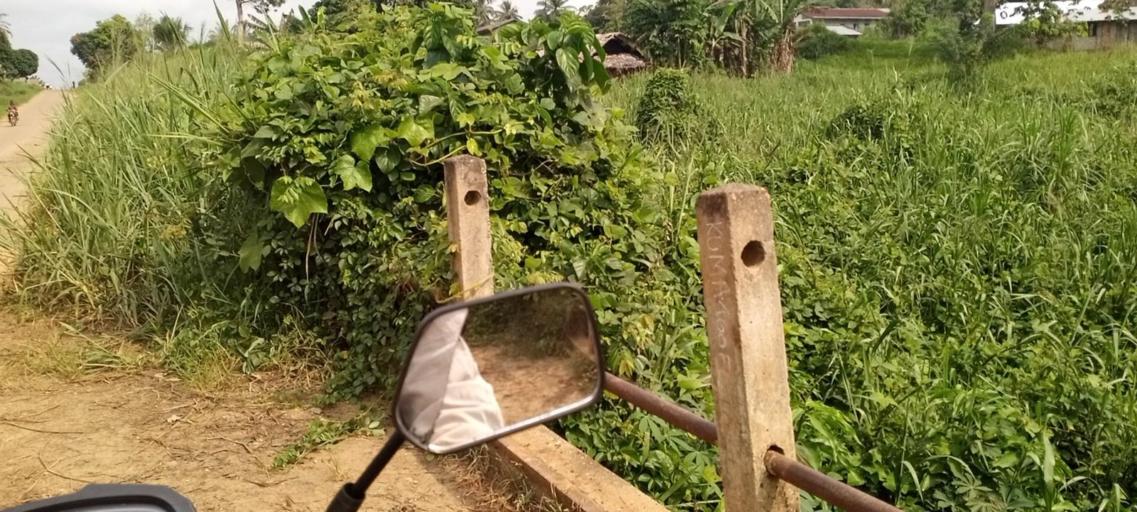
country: CD
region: Eastern Province
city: Kisangani
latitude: 0.3800
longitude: 25.3926
